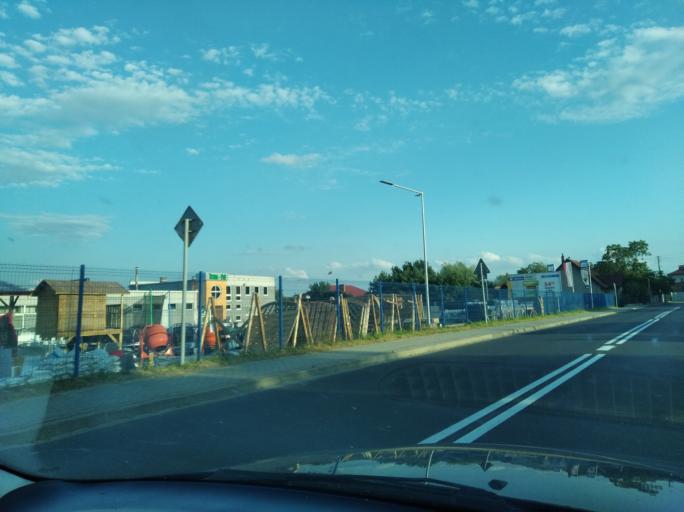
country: PL
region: Subcarpathian Voivodeship
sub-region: Powiat lezajski
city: Lezajsk
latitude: 50.2731
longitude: 22.4258
